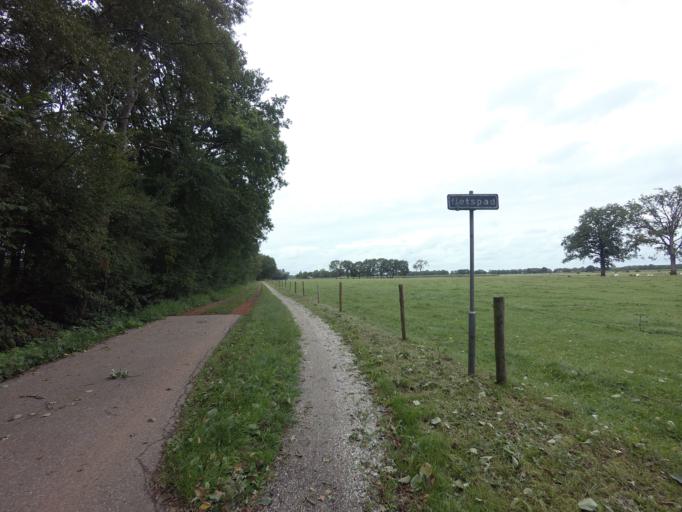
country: NL
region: Friesland
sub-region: Gemeente Weststellingwerf
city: Steggerda
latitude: 52.8904
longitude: 6.0921
